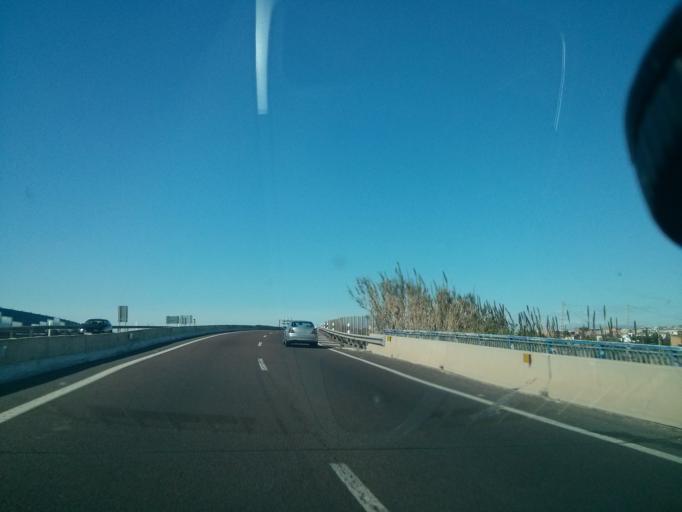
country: ES
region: Valencia
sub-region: Provincia de Valencia
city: Alboraya
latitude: 39.4957
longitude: -0.3279
